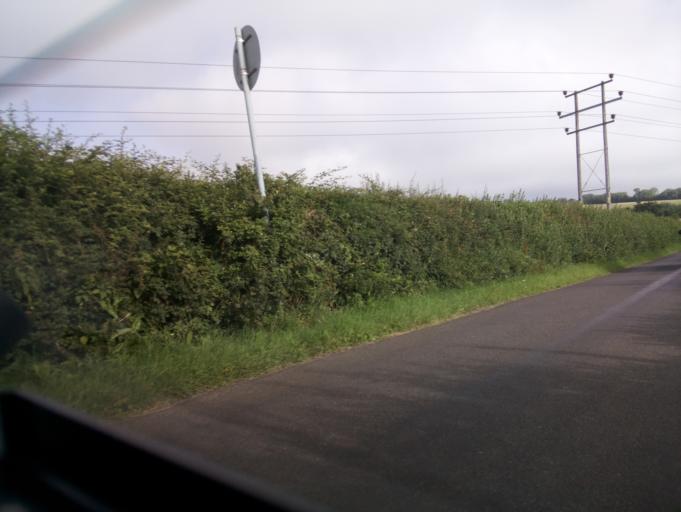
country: GB
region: England
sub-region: Borough of Swindon
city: Hannington
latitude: 51.6212
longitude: -1.7436
